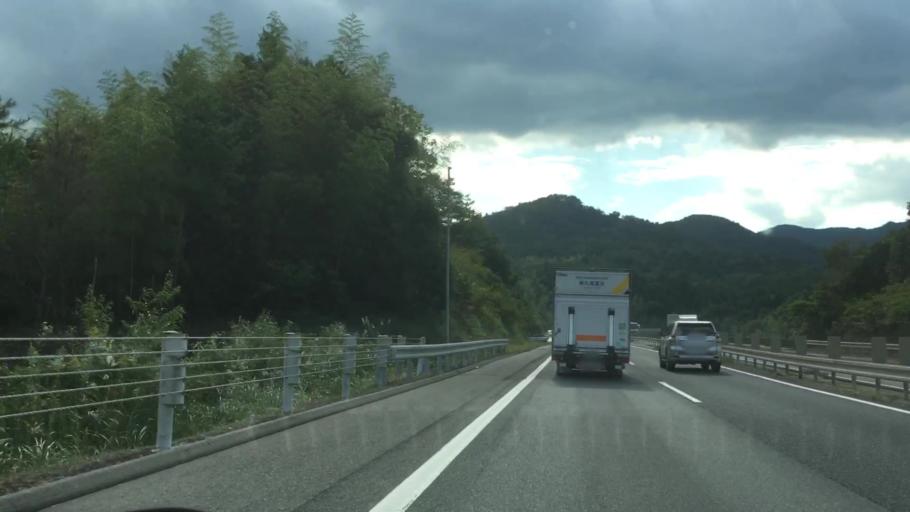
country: JP
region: Yamaguchi
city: Iwakuni
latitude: 34.1416
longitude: 132.1215
